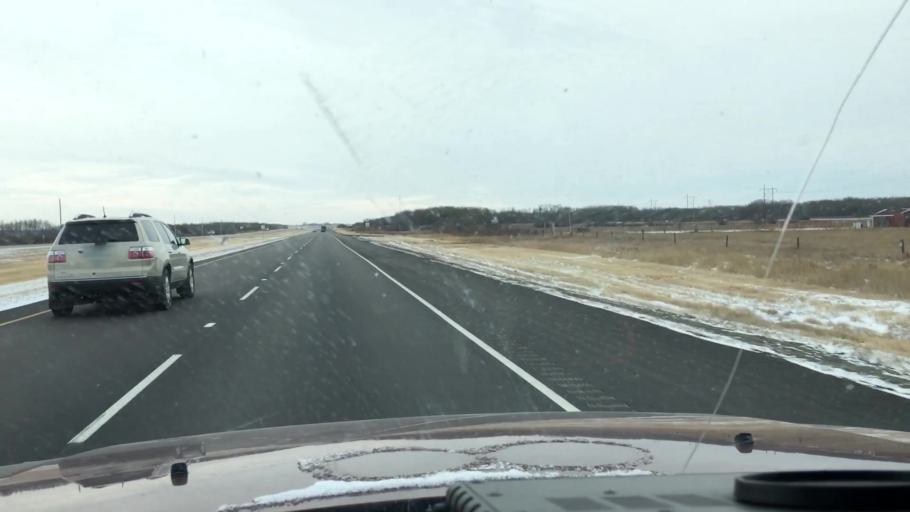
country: CA
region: Saskatchewan
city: Saskatoon
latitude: 51.8836
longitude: -106.5137
